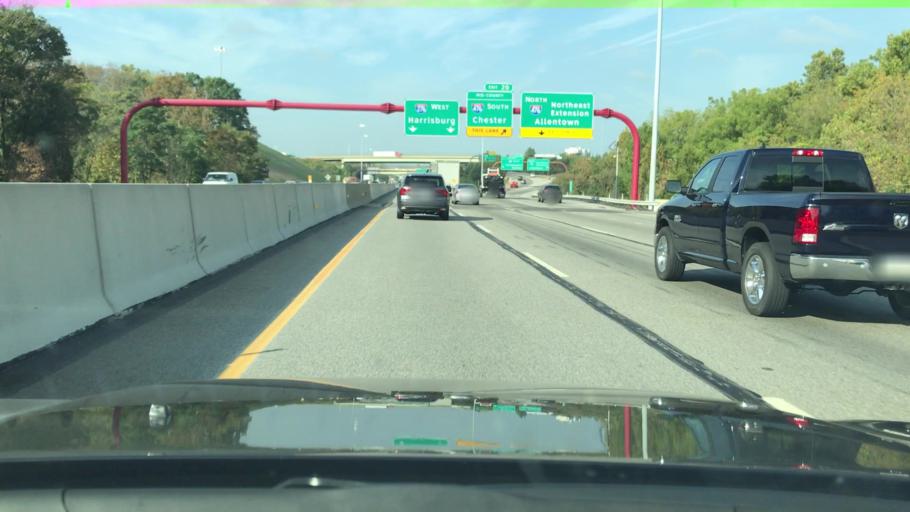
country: US
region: Pennsylvania
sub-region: Montgomery County
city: Plymouth Meeting
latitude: 40.1140
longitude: -75.2712
